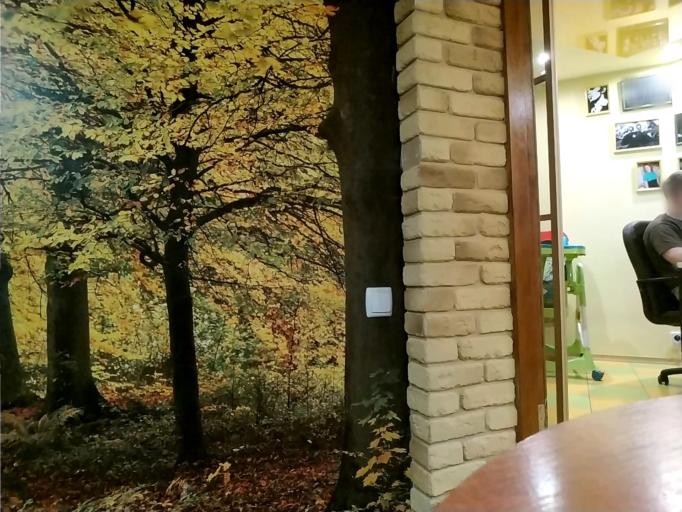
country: RU
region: Tverskaya
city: Zapadnaya Dvina
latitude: 56.3263
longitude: 31.9049
